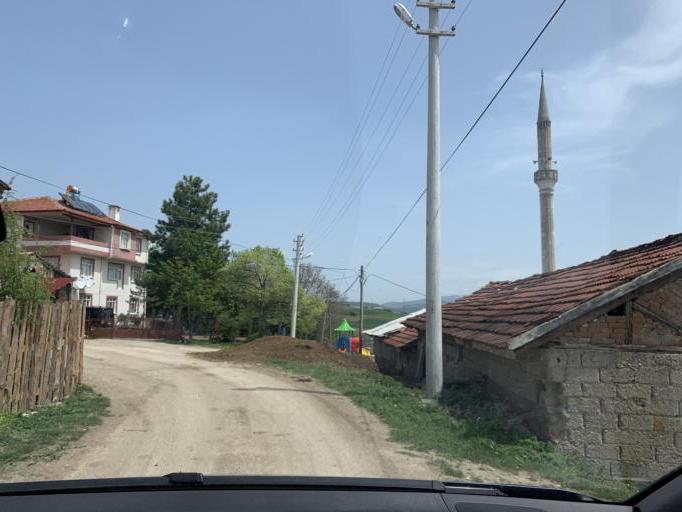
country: TR
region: Bolu
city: Bolu
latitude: 40.7669
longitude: 31.7060
